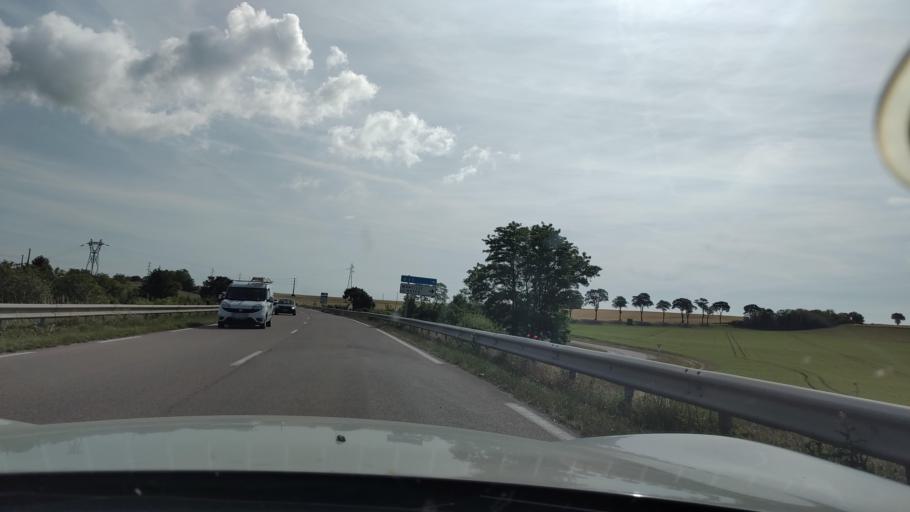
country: FR
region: Champagne-Ardenne
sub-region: Departement de l'Aube
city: Nogent-sur-Seine
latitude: 48.4837
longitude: 3.5119
